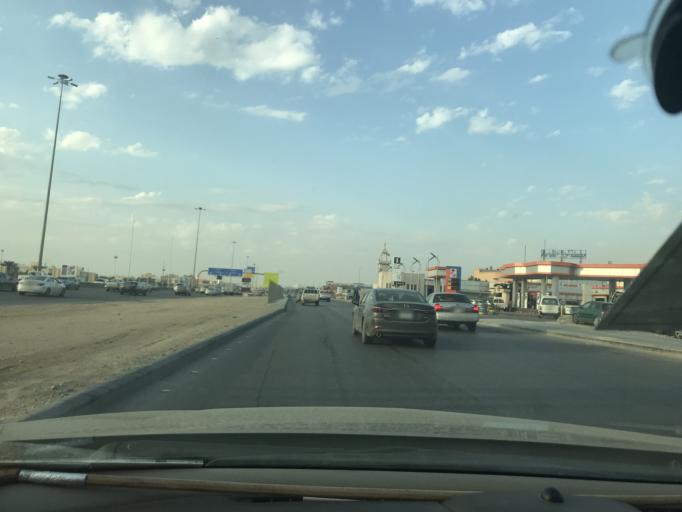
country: SA
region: Ar Riyad
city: Riyadh
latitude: 24.7464
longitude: 46.5854
